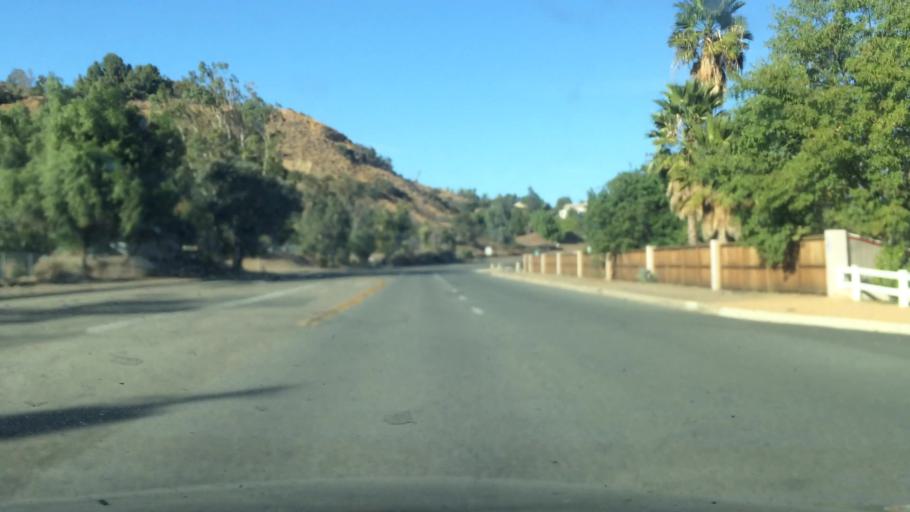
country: US
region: California
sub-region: Riverside County
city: Lakeland Village
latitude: 33.6775
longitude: -117.3985
